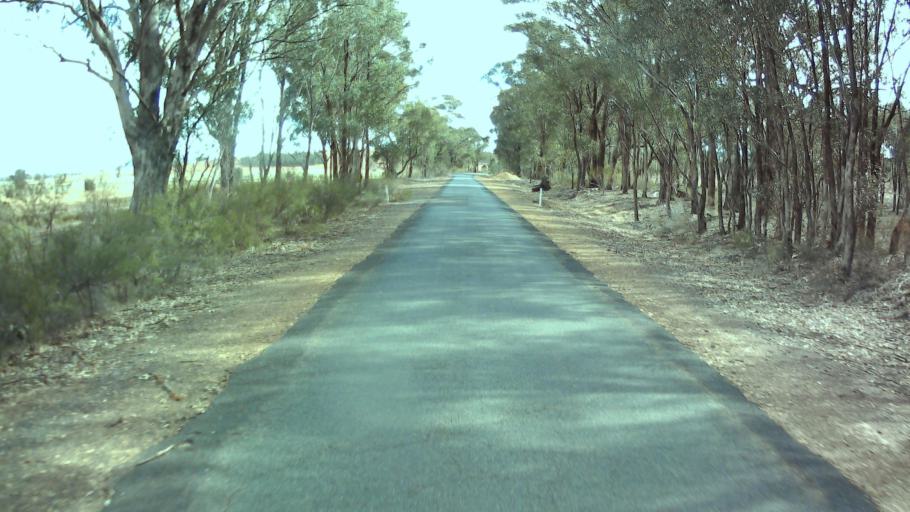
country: AU
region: New South Wales
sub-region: Weddin
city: Grenfell
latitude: -33.8464
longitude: 148.2349
